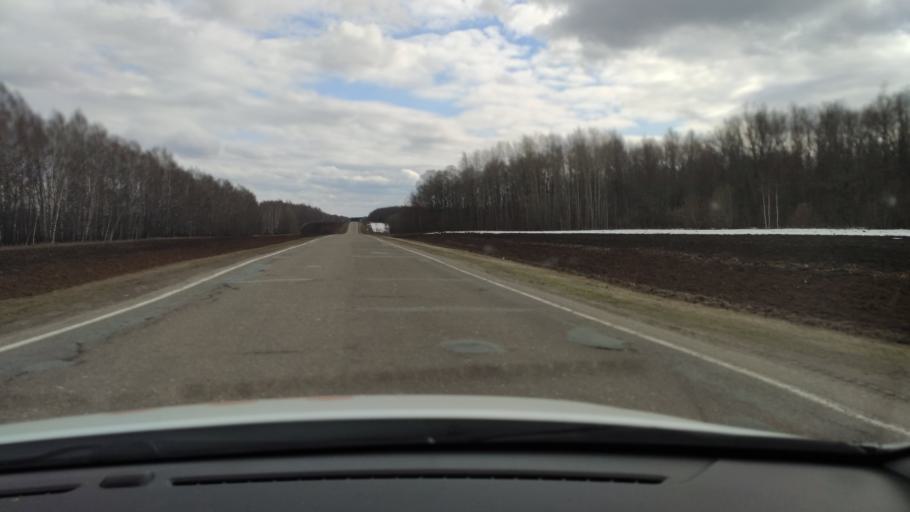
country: RU
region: Tatarstan
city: Vysokaya Gora
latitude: 56.0843
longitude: 49.1847
